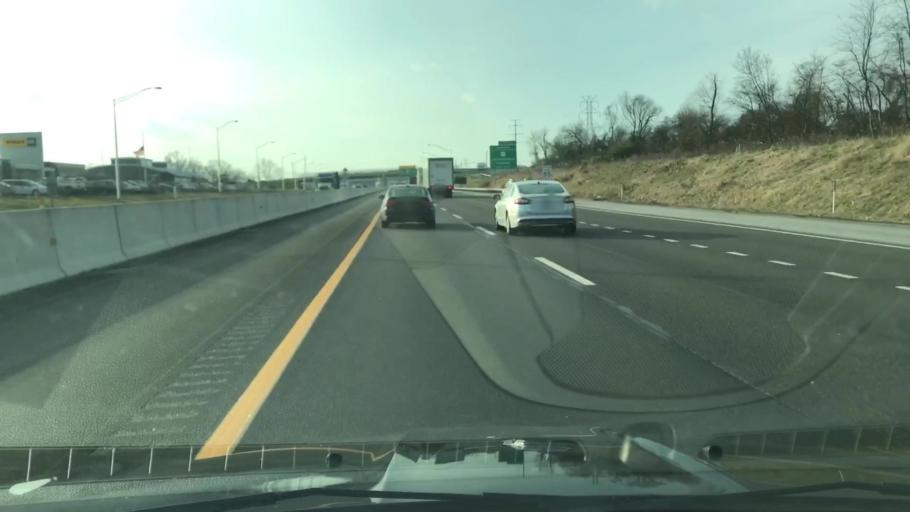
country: US
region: Pennsylvania
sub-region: Bucks County
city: Hulmeville
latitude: 40.1283
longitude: -74.9369
